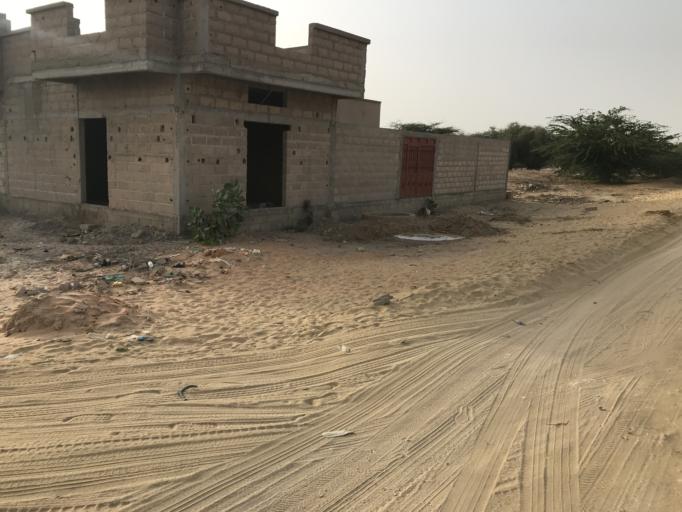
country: SN
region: Saint-Louis
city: Saint-Louis
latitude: 16.0323
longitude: -16.4446
